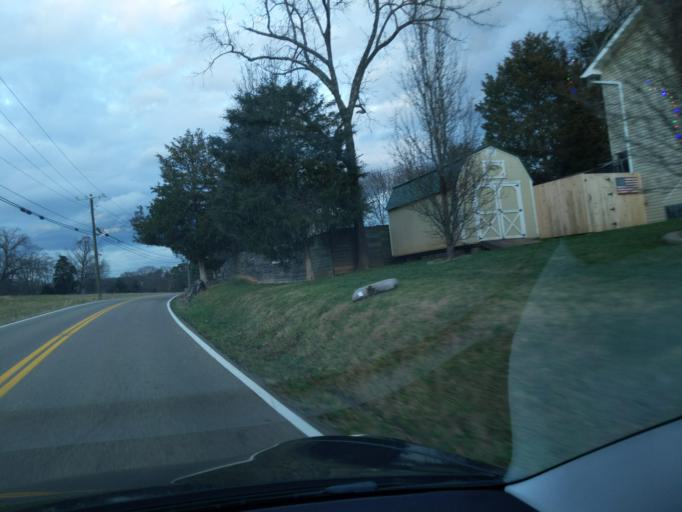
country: US
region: Tennessee
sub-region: Jefferson County
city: Dandridge
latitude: 36.0303
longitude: -83.4109
